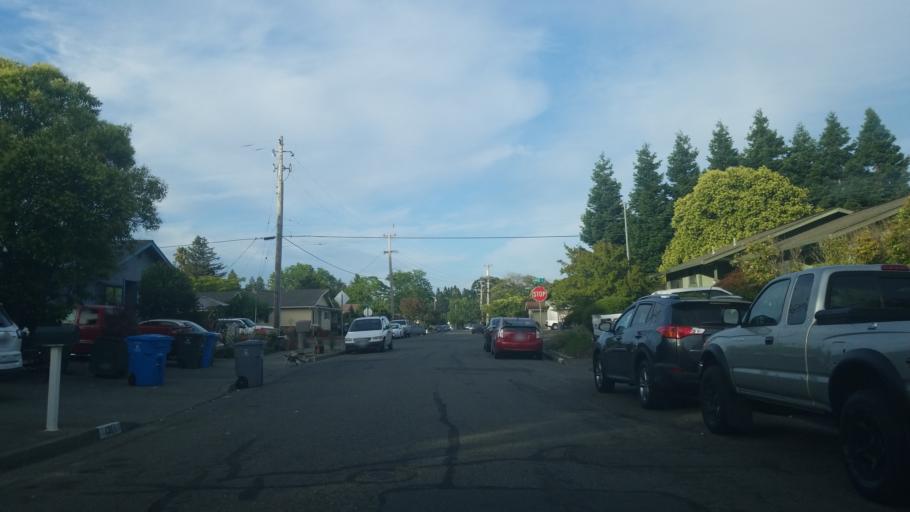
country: US
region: California
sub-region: Sonoma County
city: Santa Rosa
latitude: 38.4536
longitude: -122.7396
